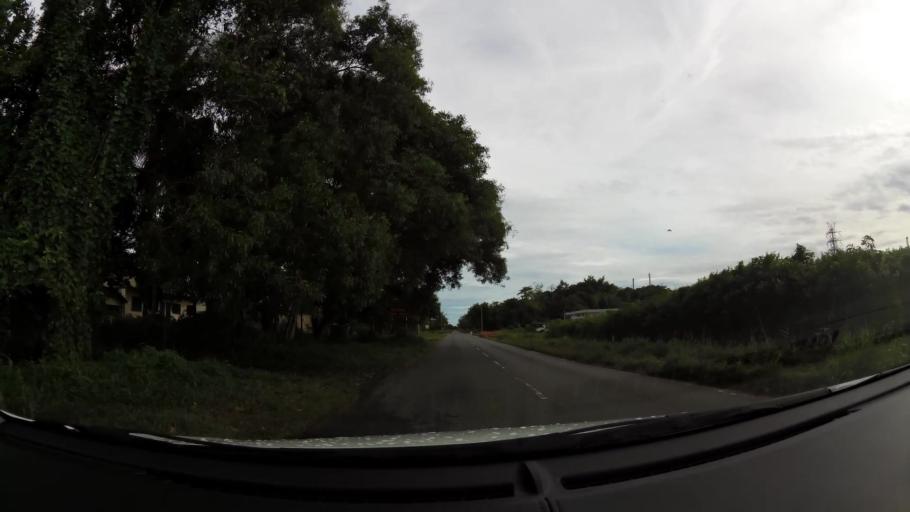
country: BN
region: Belait
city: Seria
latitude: 4.6134
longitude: 114.3389
